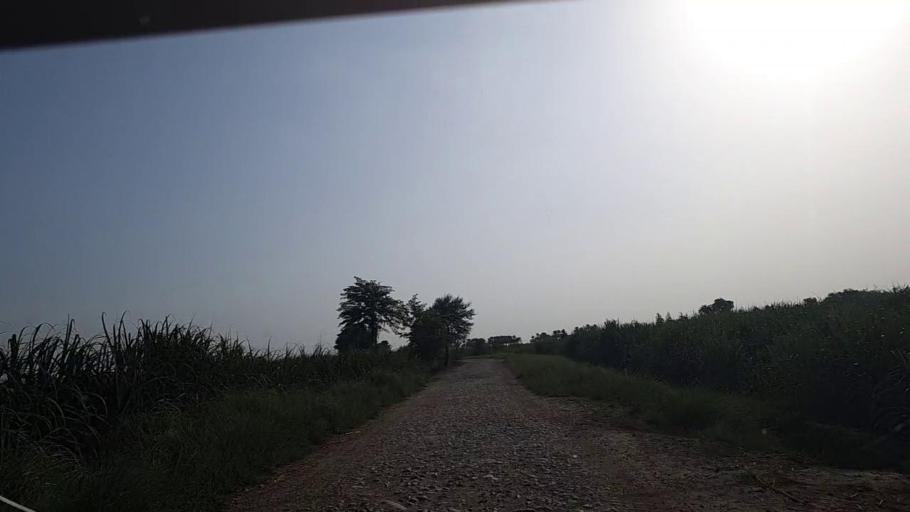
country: PK
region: Sindh
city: Ghotki
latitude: 27.9871
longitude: 69.2574
